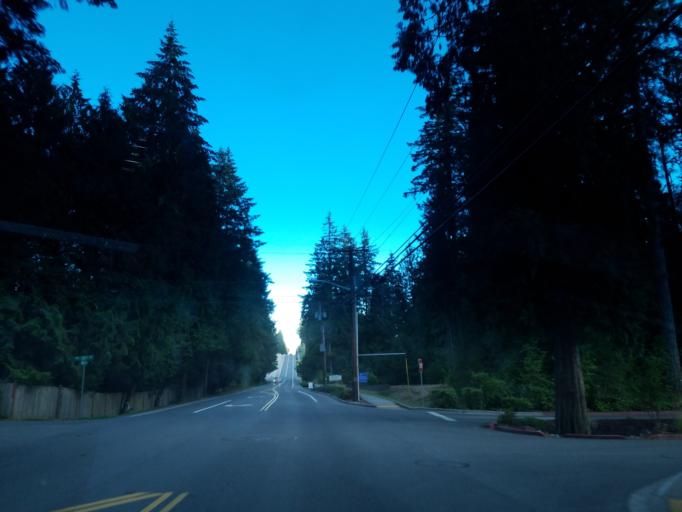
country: US
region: Washington
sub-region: King County
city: City of Sammamish
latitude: 47.6261
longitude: -122.0139
